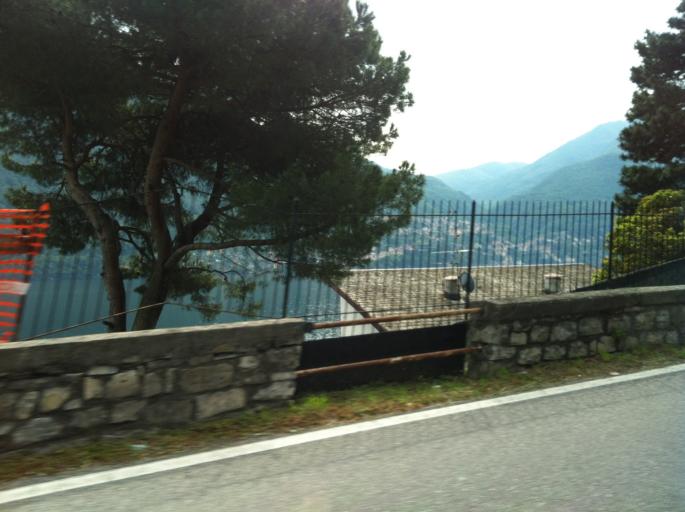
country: IT
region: Lombardy
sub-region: Provincia di Como
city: Brienno
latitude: 45.9234
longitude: 9.1313
